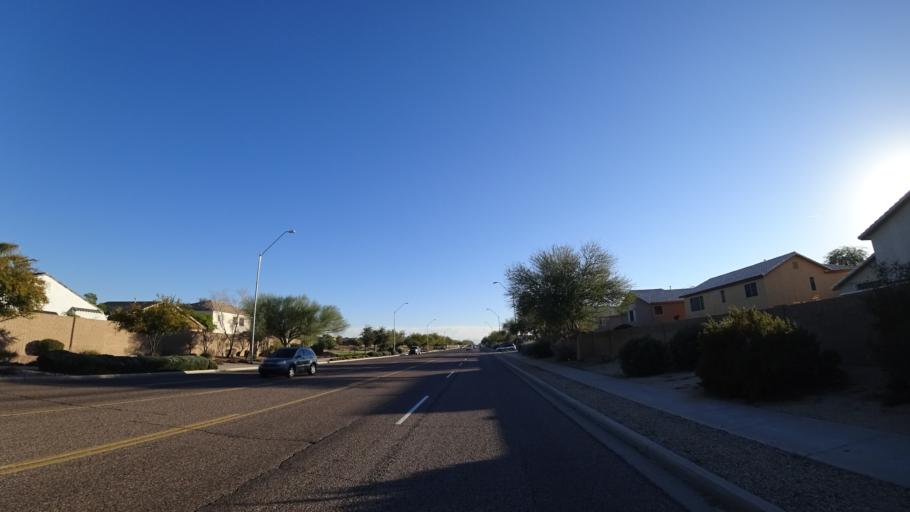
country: US
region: Arizona
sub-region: Maricopa County
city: Sun City West
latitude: 33.6791
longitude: -112.2899
